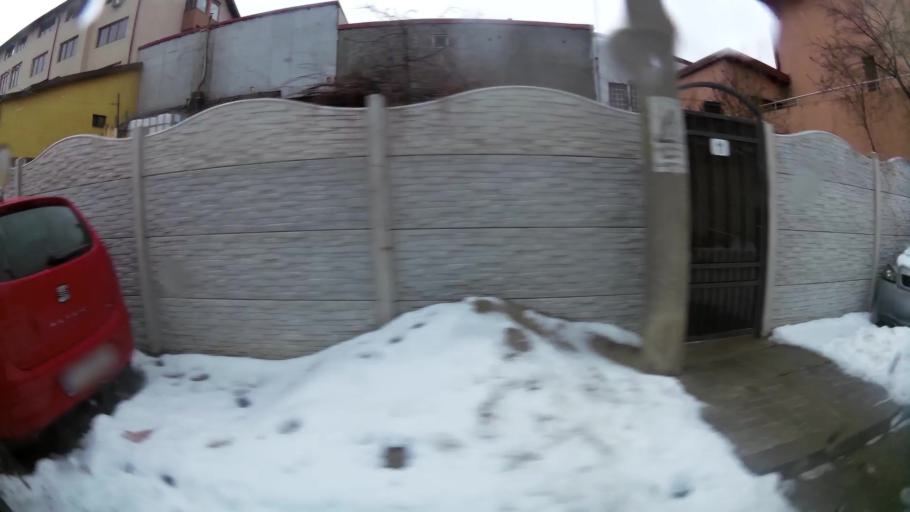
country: RO
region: Ilfov
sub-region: Comuna Chiajna
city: Rosu
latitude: 44.4278
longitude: 26.0123
